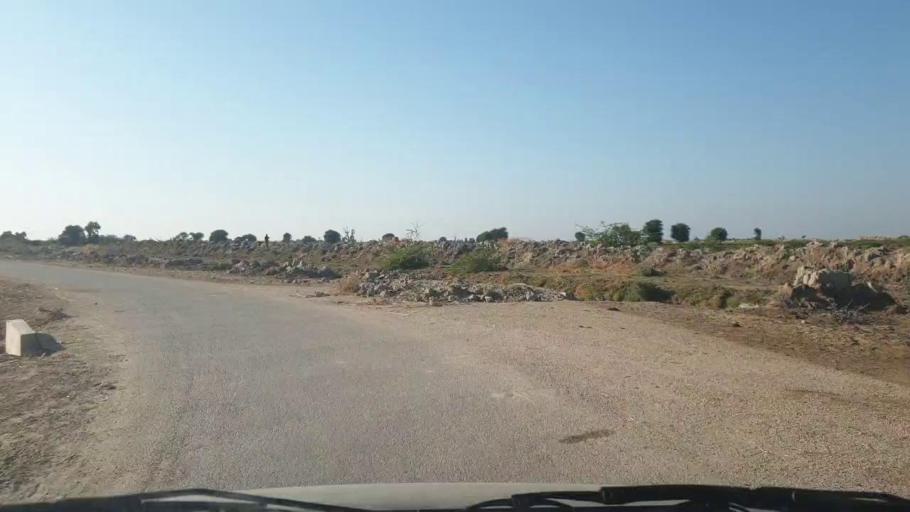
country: PK
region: Sindh
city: Samaro
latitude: 25.3516
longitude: 69.2983
